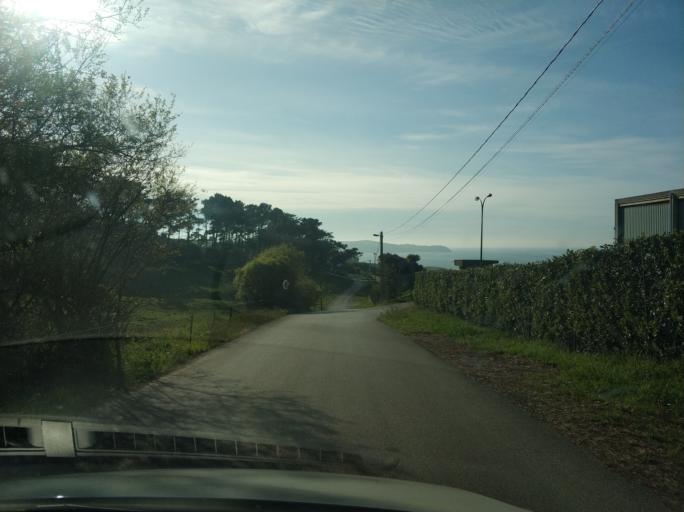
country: ES
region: Cantabria
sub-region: Provincia de Cantabria
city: Comillas
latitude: 43.3888
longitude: -4.3001
